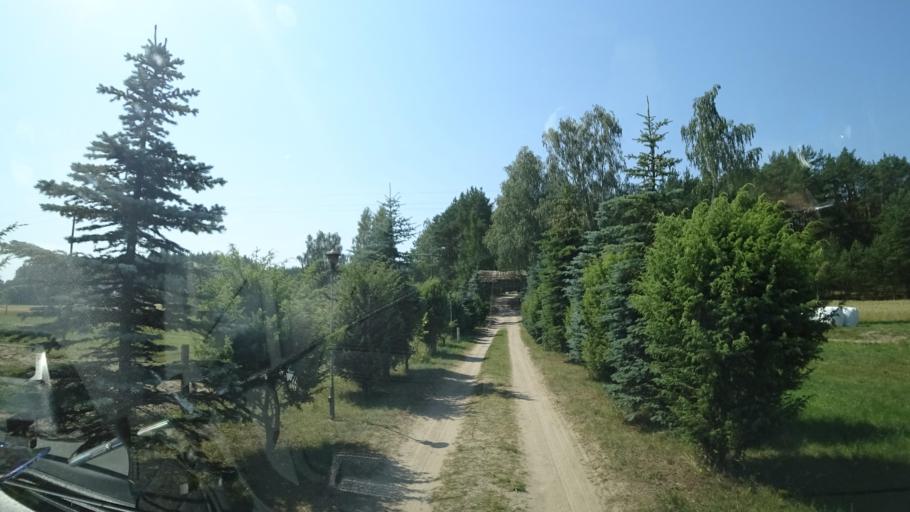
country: PL
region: Pomeranian Voivodeship
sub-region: Powiat chojnicki
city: Brusy
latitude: 53.8691
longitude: 17.5468
